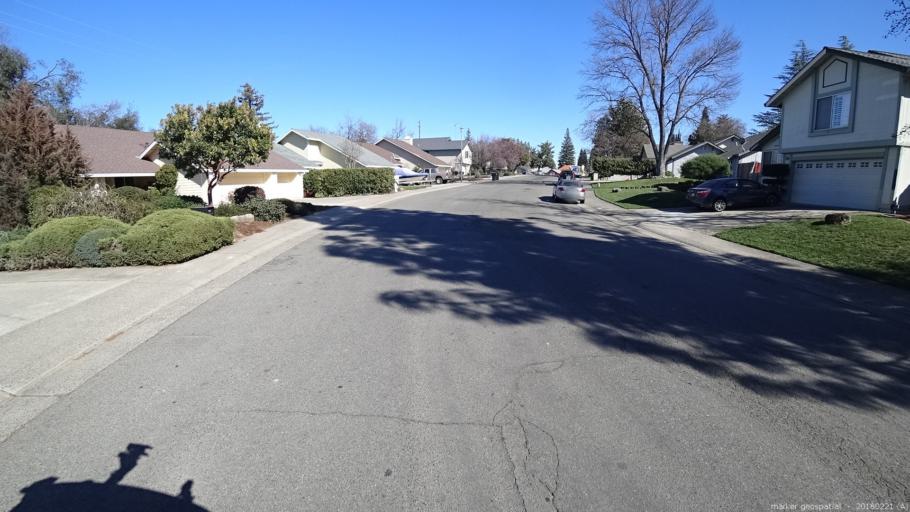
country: US
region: California
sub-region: Sacramento County
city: Citrus Heights
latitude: 38.6854
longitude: -121.2615
